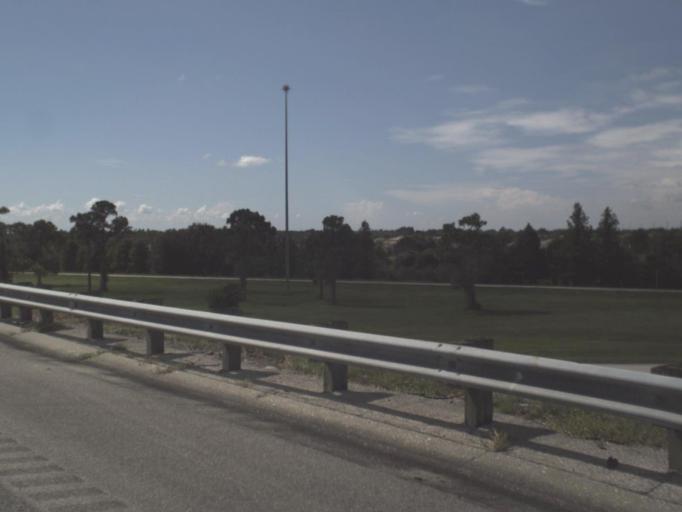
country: US
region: Florida
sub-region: Charlotte County
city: Charlotte Park
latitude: 26.8955
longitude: -82.0030
